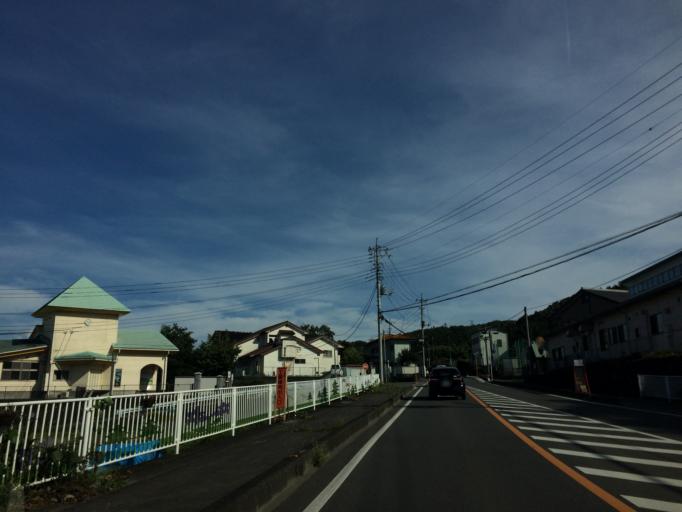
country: JP
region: Gunma
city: Nakanojomachi
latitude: 36.5465
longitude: 138.9246
